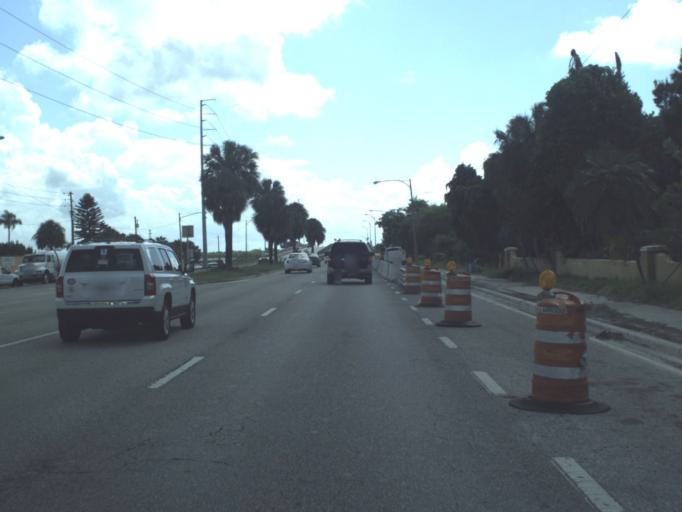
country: US
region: Florida
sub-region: Pinellas County
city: Bay Pines
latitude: 27.8136
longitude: -82.7684
